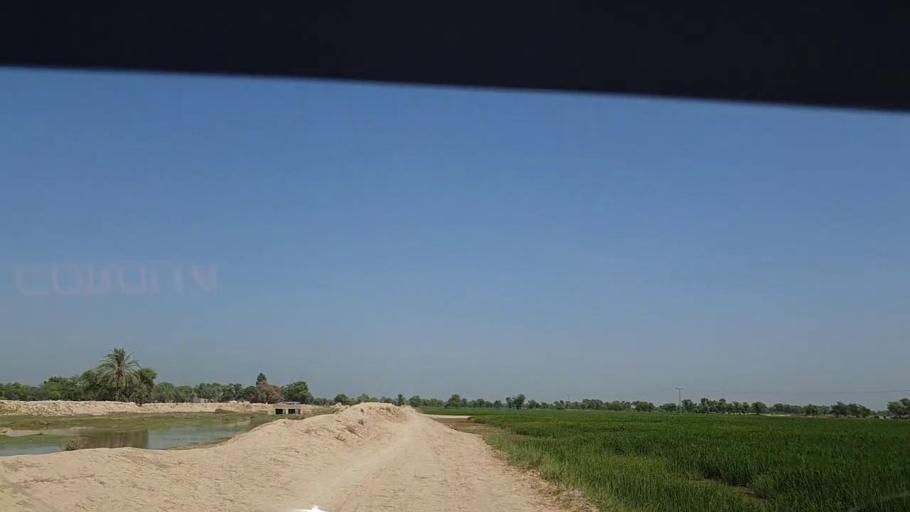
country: PK
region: Sindh
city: Tangwani
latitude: 28.2881
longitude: 69.0412
